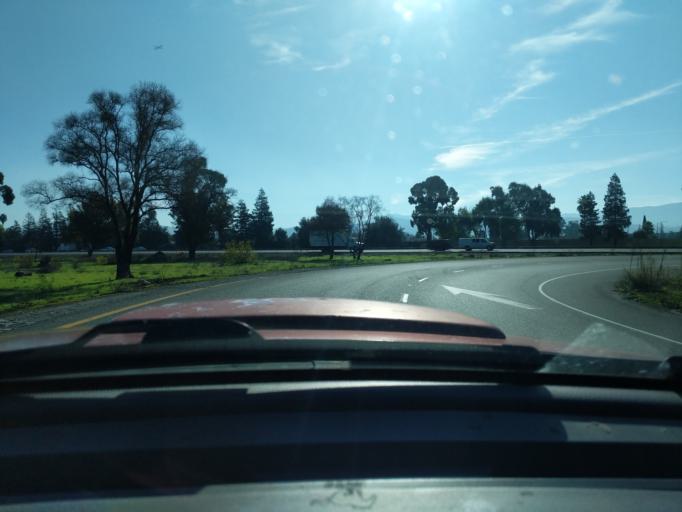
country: US
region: California
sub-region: Santa Clara County
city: Seven Trees
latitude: 37.2566
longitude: -121.7933
